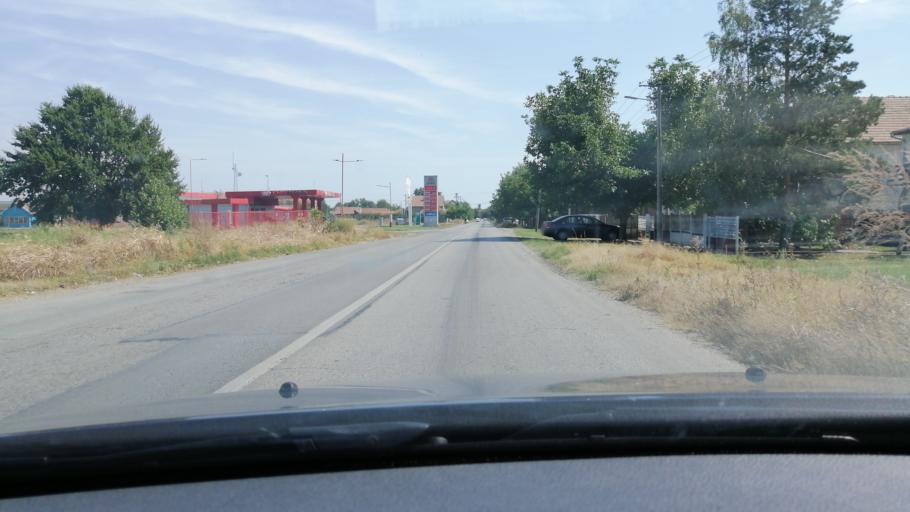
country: RS
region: Autonomna Pokrajina Vojvodina
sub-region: Srednjebanatski Okrug
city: Secanj
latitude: 45.3690
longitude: 20.7597
